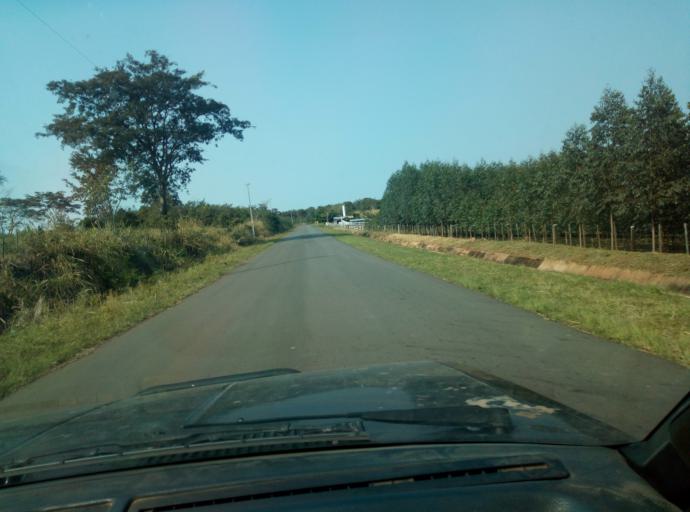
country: PY
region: Caaguazu
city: Carayao
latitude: -25.1995
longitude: -56.3083
